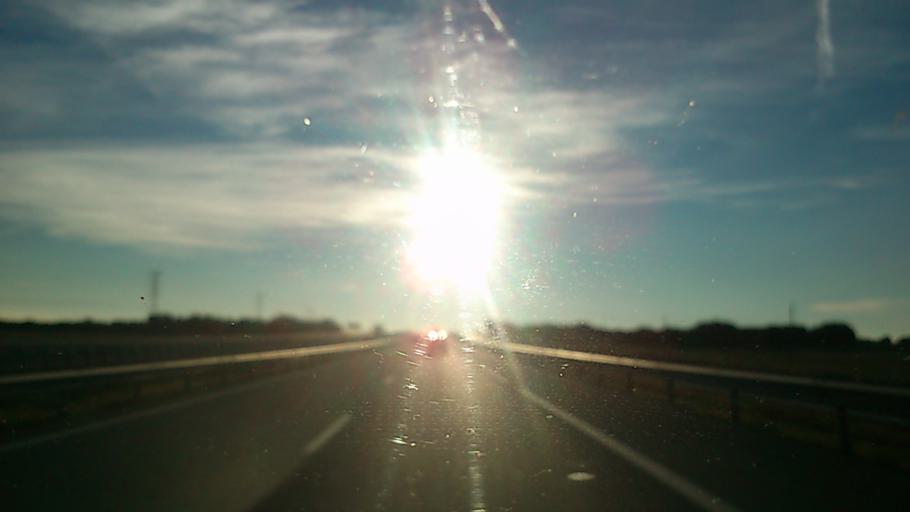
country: ES
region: Castille-La Mancha
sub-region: Provincia de Guadalajara
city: Gajanejos
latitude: 40.8320
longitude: -2.9073
